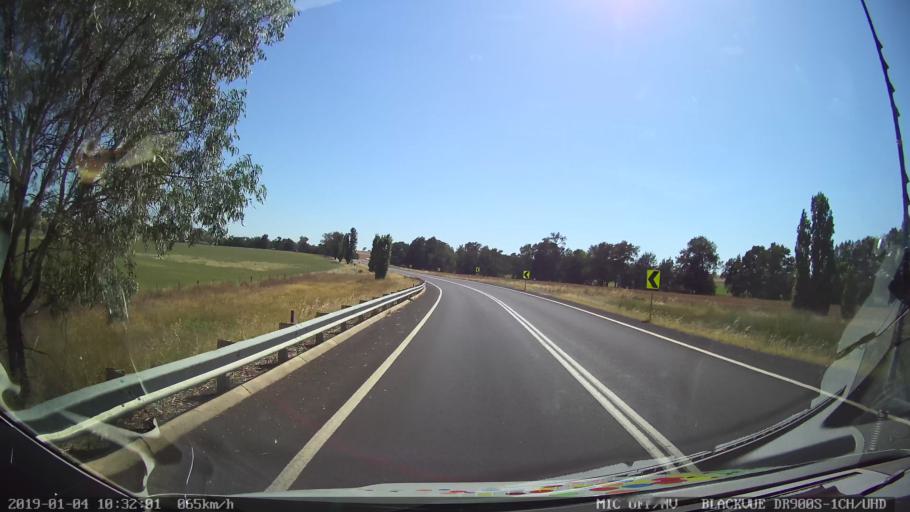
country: AU
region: New South Wales
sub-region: Cabonne
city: Canowindra
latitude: -33.3298
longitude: 148.6355
